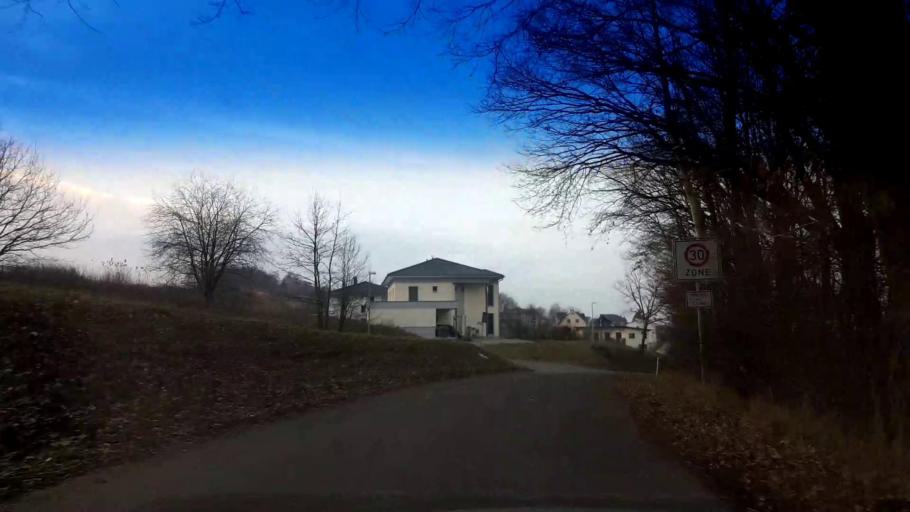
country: DE
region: Bavaria
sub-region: Upper Franconia
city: Hirschaid
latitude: 49.8023
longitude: 10.9889
